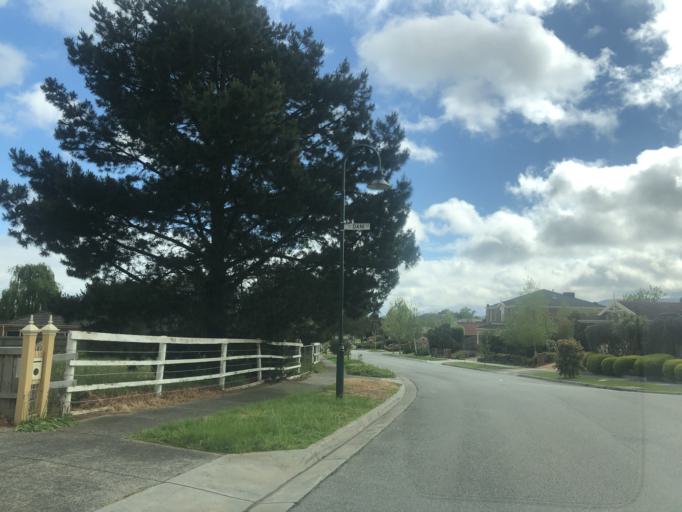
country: AU
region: Victoria
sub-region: Knox
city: Rowville
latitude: -37.9361
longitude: 145.2545
